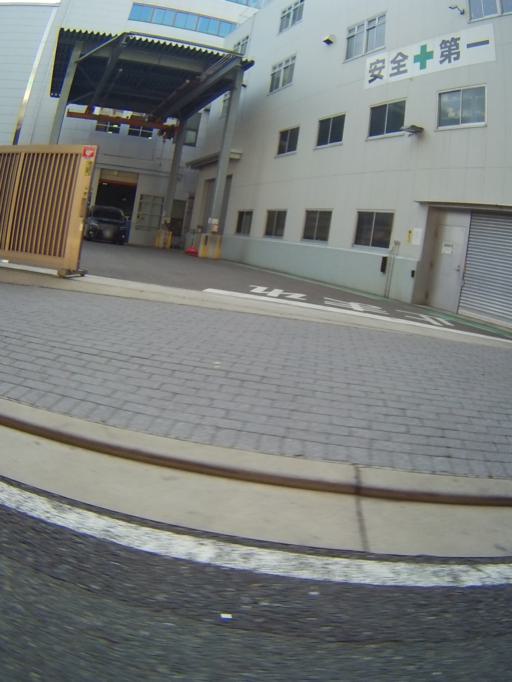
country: JP
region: Osaka
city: Osaka-shi
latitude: 34.6586
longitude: 135.4681
